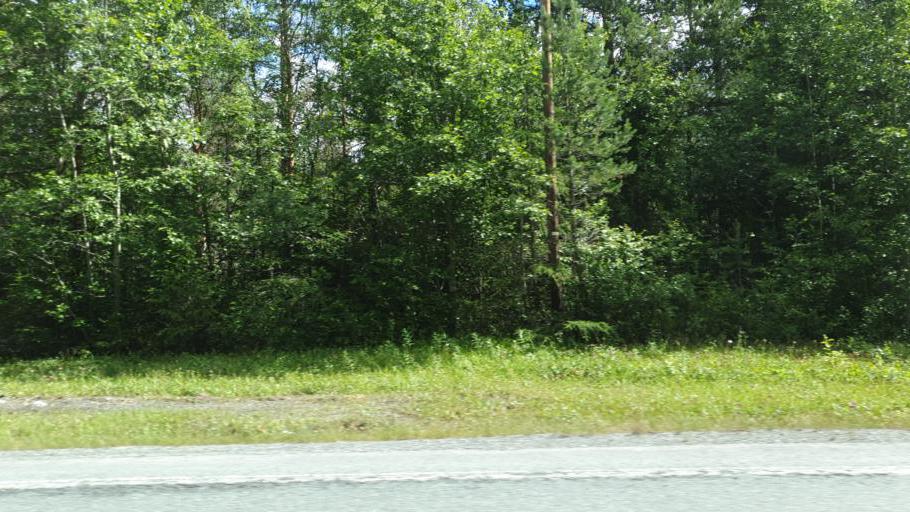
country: NO
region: Sor-Trondelag
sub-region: Rennebu
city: Berkak
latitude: 62.7079
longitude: 9.9542
